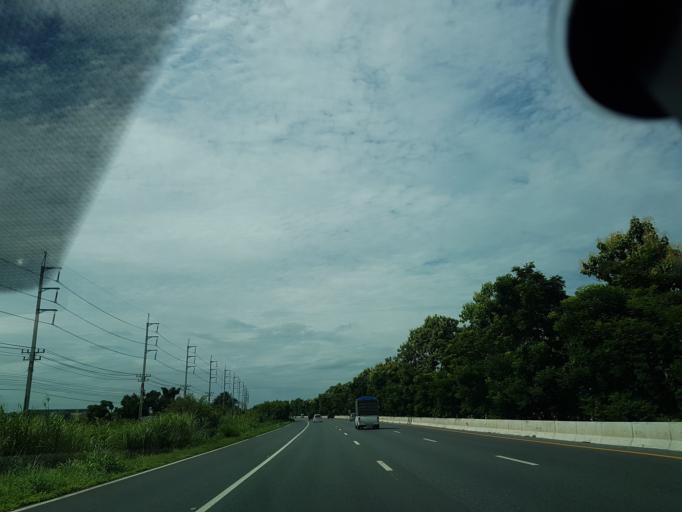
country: TH
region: Ang Thong
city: Chaiyo
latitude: 14.7012
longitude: 100.4562
